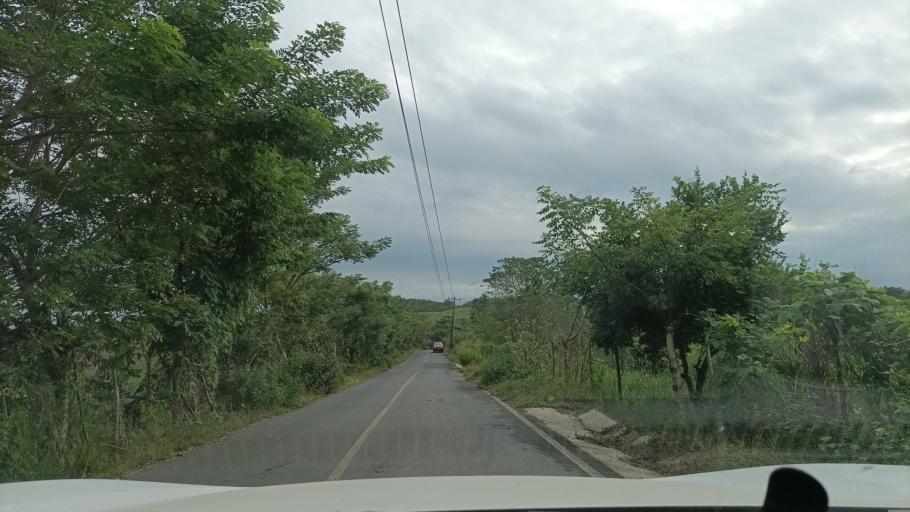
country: MX
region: Veracruz
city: Hidalgotitlan
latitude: 17.6879
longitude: -94.4484
